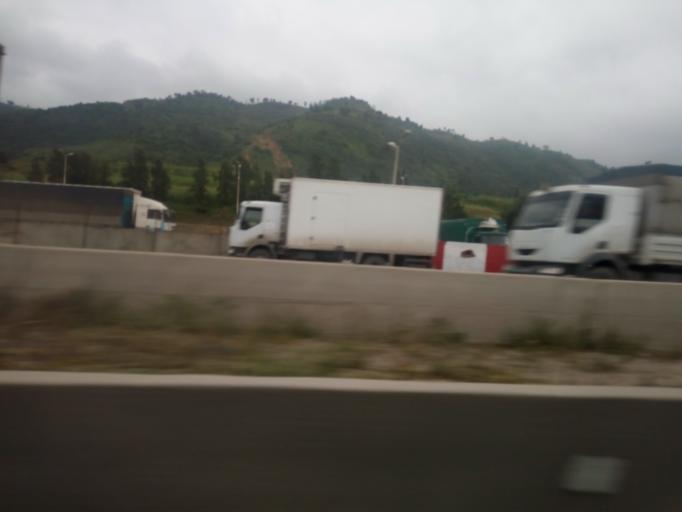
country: DZ
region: Bouira
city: Lakhdaria
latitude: 36.5540
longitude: 3.5931
